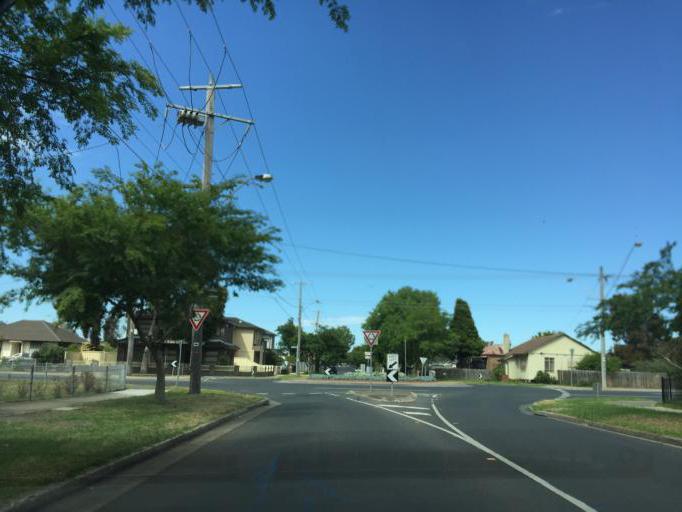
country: AU
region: Victoria
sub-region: Maribyrnong
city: Braybrook
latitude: -37.7855
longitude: 144.8588
